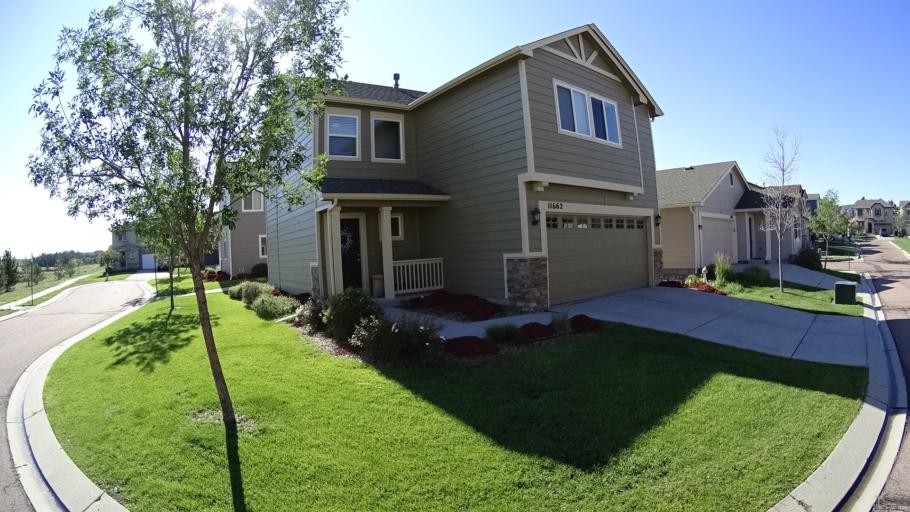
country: US
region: Colorado
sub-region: El Paso County
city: Gleneagle
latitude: 38.9992
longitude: -104.7938
